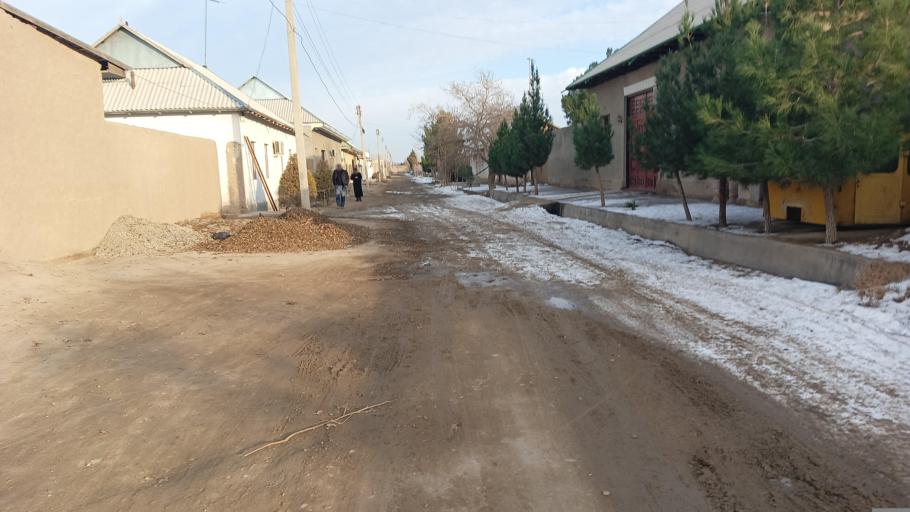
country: UZ
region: Qashqadaryo
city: Yangi Mirishkor
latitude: 38.8926
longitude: 65.3049
